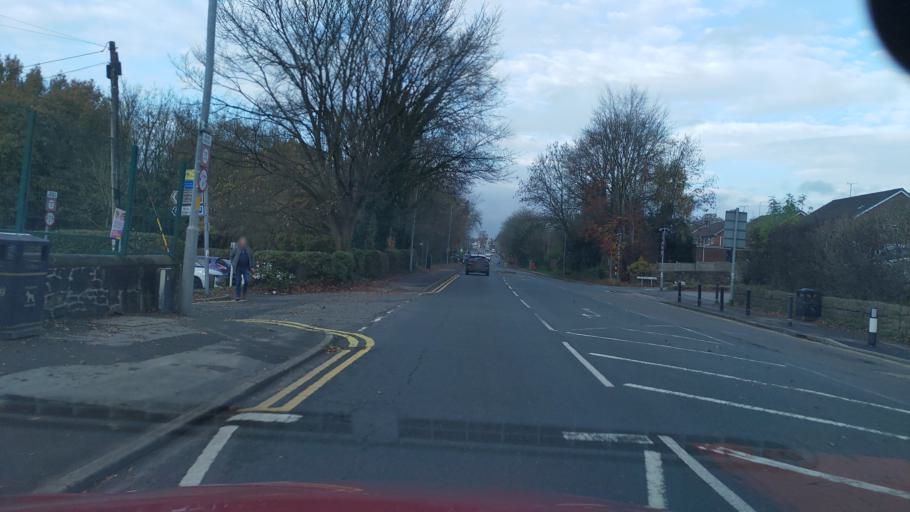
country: GB
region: England
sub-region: Lancashire
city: Clayton-le-Woods
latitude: 53.6894
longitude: -2.6391
